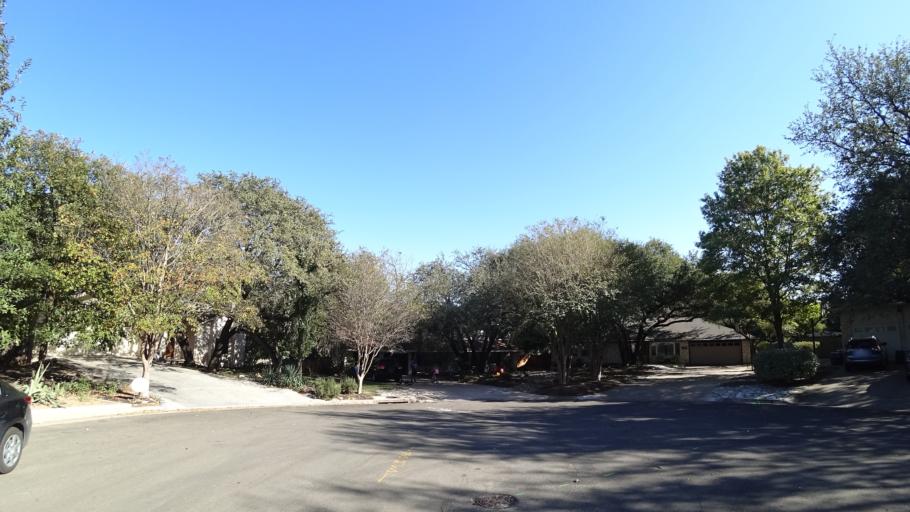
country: US
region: Texas
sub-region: Williamson County
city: Jollyville
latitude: 30.4178
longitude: -97.7675
